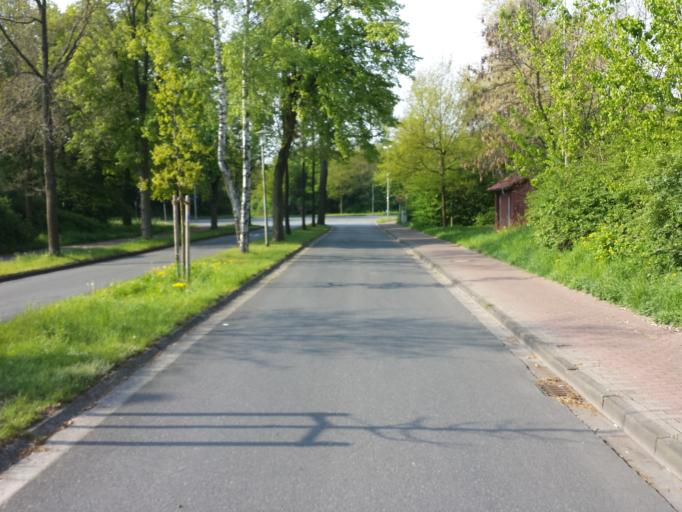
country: DE
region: North Rhine-Westphalia
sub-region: Regierungsbezirk Detmold
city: Guetersloh
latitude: 51.8832
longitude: 8.3676
